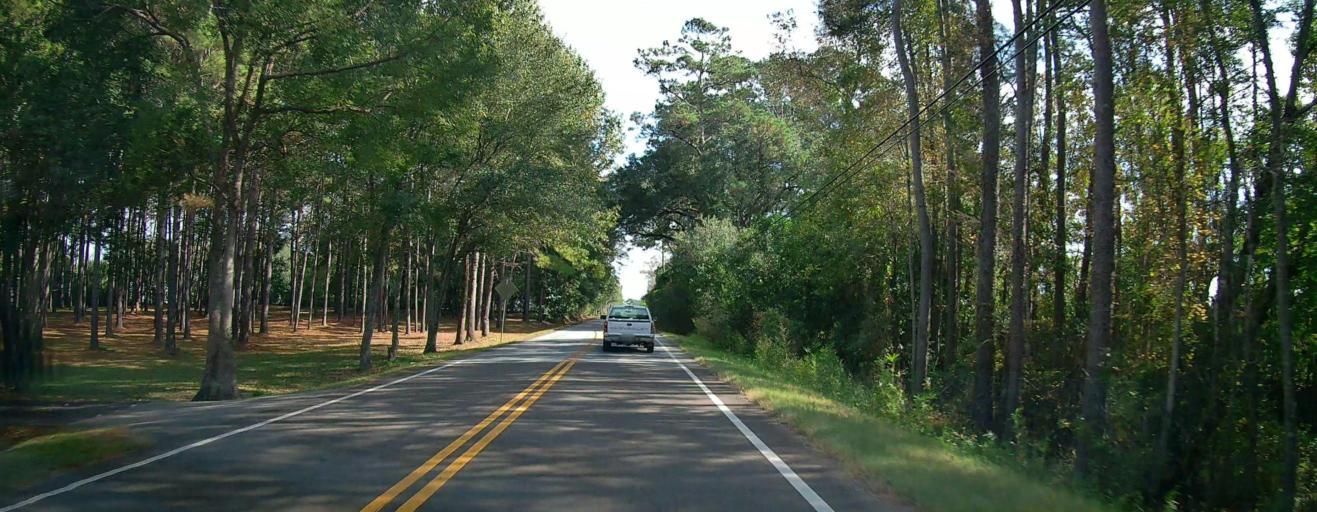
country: US
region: Georgia
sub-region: Thomas County
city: Thomasville
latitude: 30.8754
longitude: -84.0056
